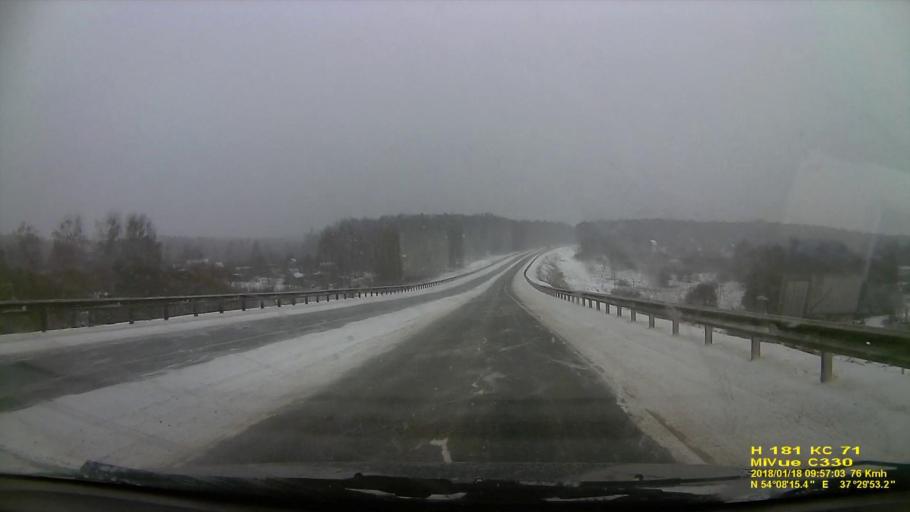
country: RU
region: Tula
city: Kosaya Gora
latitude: 54.1375
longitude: 37.4981
